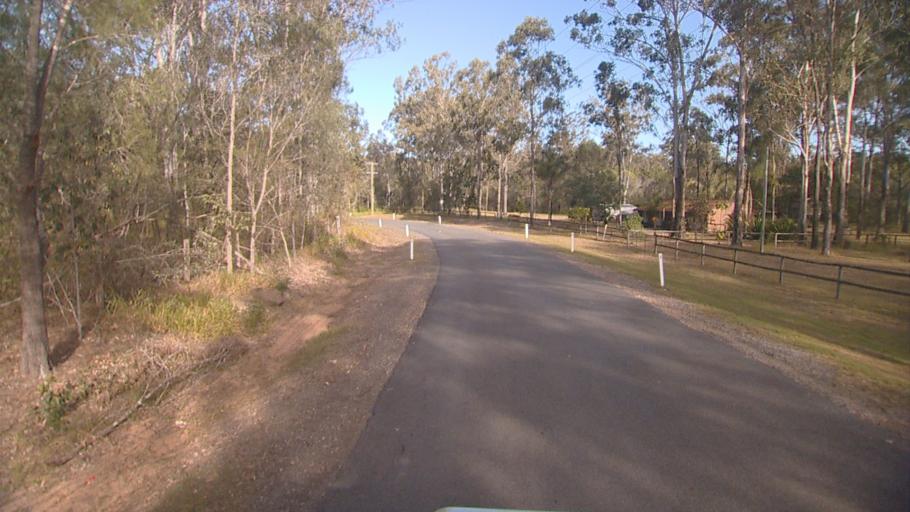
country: AU
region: Queensland
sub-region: Logan
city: Cedar Vale
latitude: -27.8261
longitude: 153.0663
